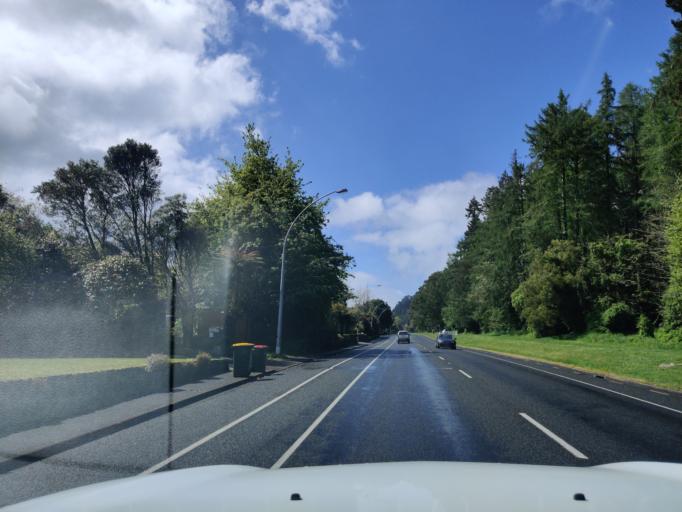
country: NZ
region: Bay of Plenty
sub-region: Rotorua District
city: Rotorua
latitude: -38.1522
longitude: 176.2848
